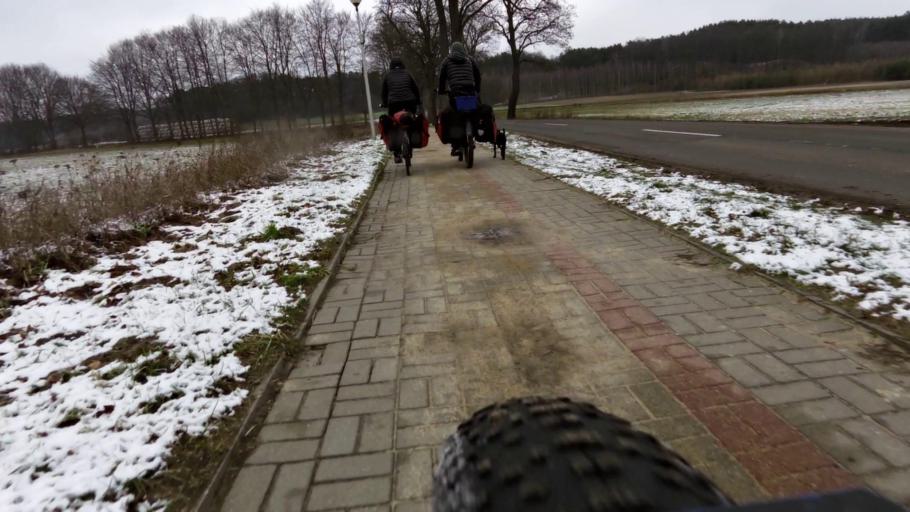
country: PL
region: West Pomeranian Voivodeship
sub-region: Powiat walecki
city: Miroslawiec
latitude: 53.3527
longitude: 16.0859
